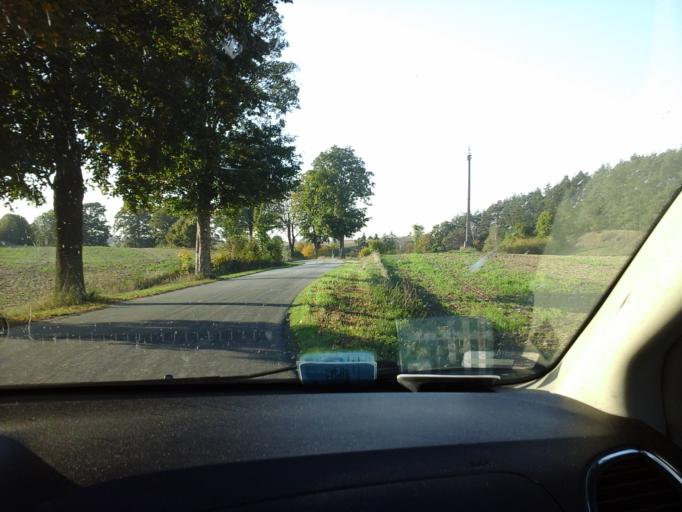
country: PL
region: Kujawsko-Pomorskie
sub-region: Powiat brodnicki
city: Brzozie
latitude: 53.2944
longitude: 19.6491
